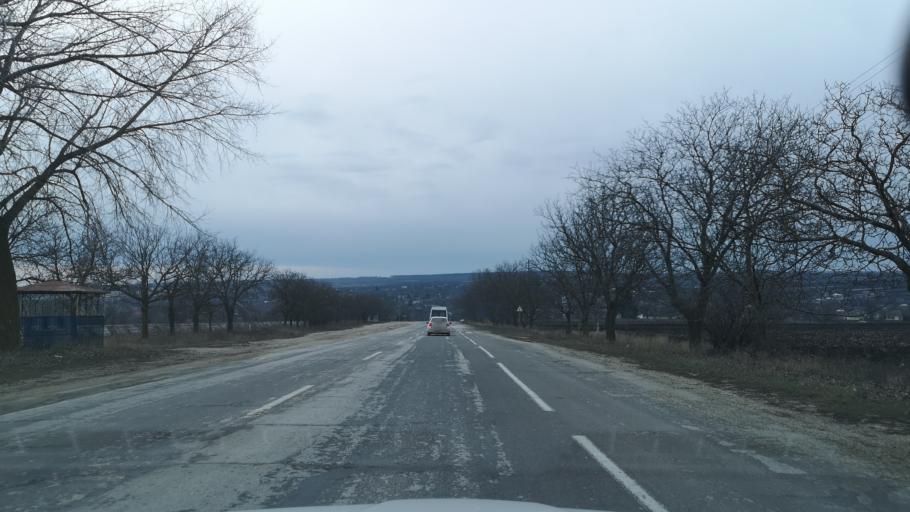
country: RO
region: Botosani
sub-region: Comuna Radauti-Prut
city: Miorcani
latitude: 48.3044
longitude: 26.9456
